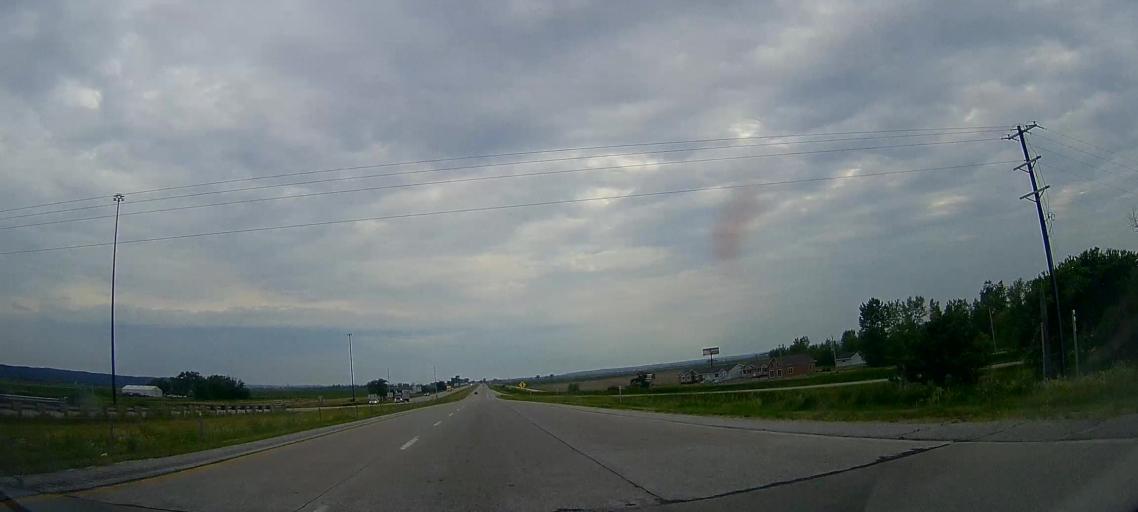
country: US
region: Iowa
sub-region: Harrison County
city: Missouri Valley
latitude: 41.5492
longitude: -95.9175
